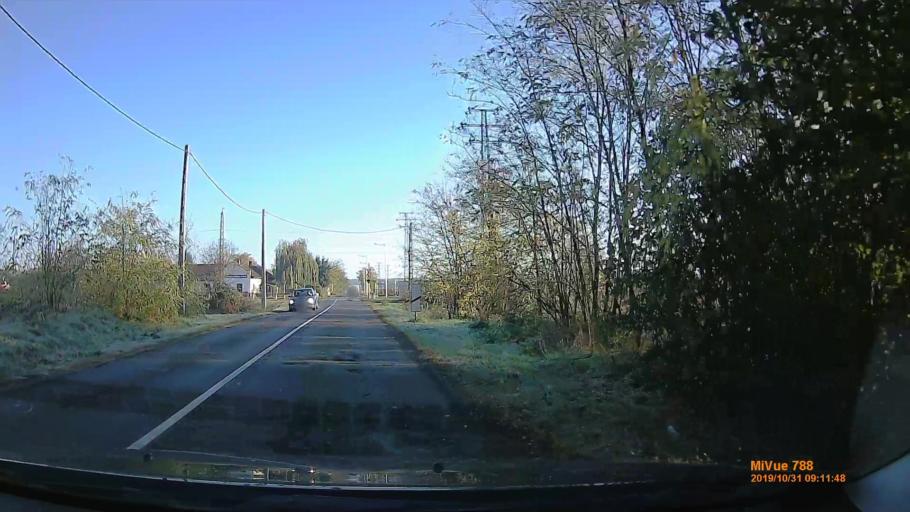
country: HU
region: Pest
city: Peteri
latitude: 47.3695
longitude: 19.3897
